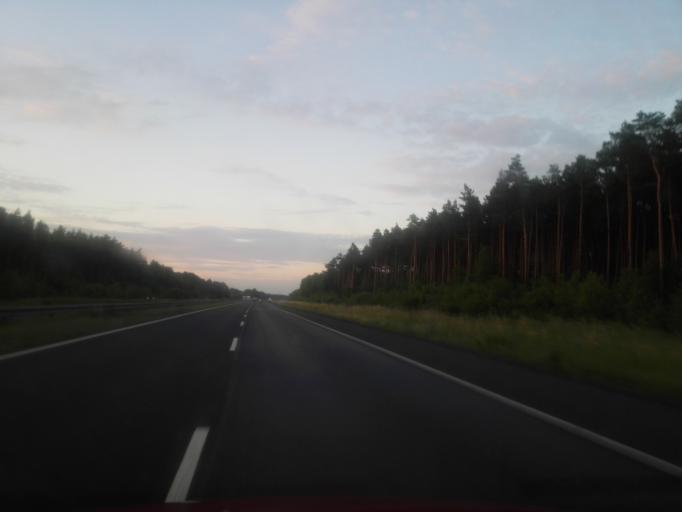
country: PL
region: Silesian Voivodeship
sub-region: Powiat czestochowski
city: Borowno
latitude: 51.0066
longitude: 19.2995
